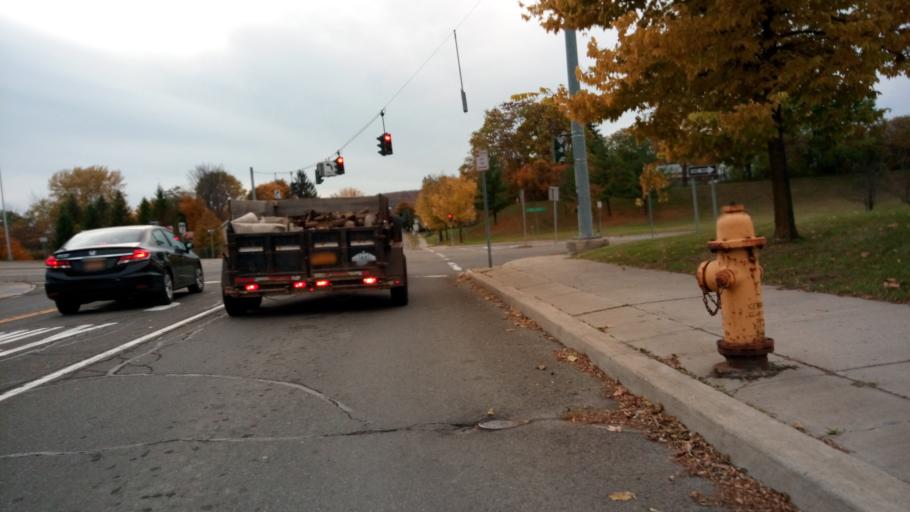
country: US
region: New York
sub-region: Chemung County
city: Elmira
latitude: 42.0748
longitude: -76.7995
